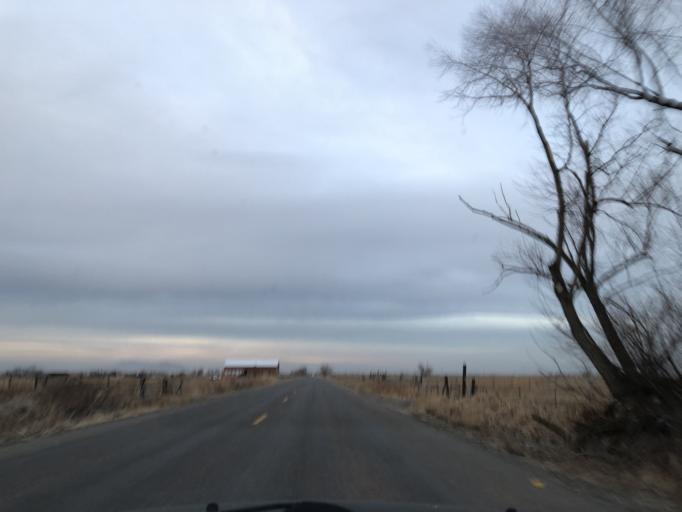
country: US
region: Utah
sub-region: Cache County
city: Benson
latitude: 41.7516
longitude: -111.9116
